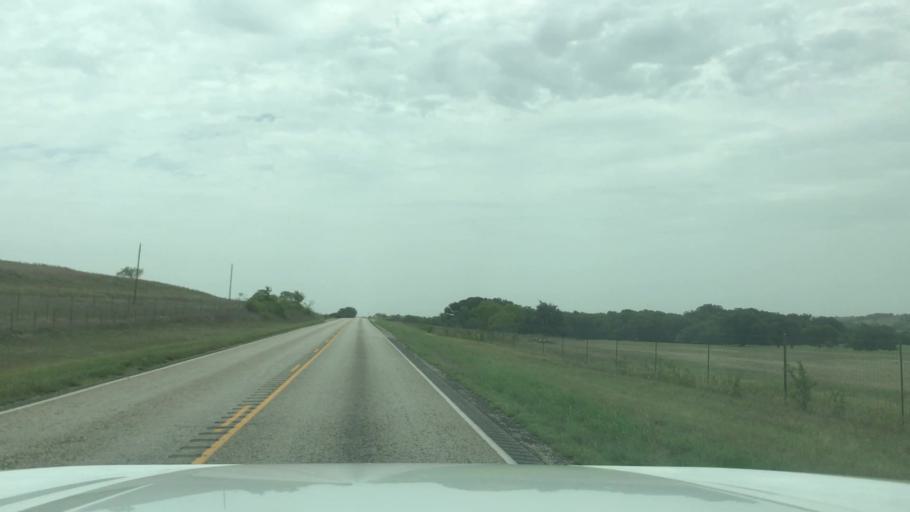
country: US
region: Texas
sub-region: Erath County
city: Dublin
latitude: 32.0567
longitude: -98.1843
